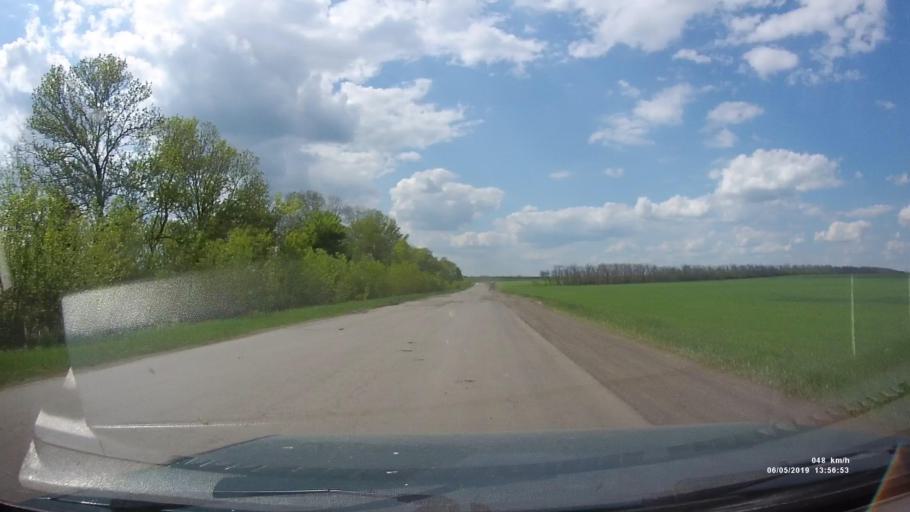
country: RU
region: Rostov
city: Melikhovskaya
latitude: 47.6827
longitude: 40.4272
